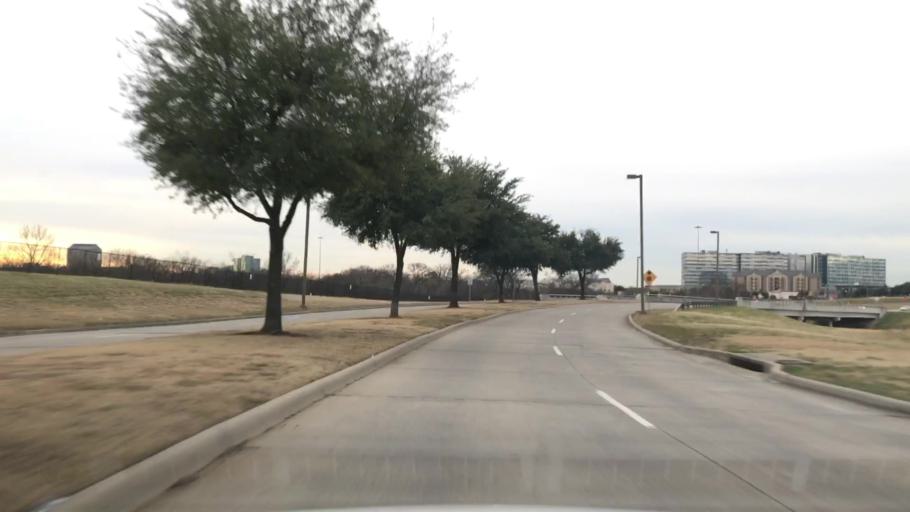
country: US
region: Texas
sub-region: Dallas County
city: Farmers Branch
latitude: 32.8904
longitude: -96.9541
